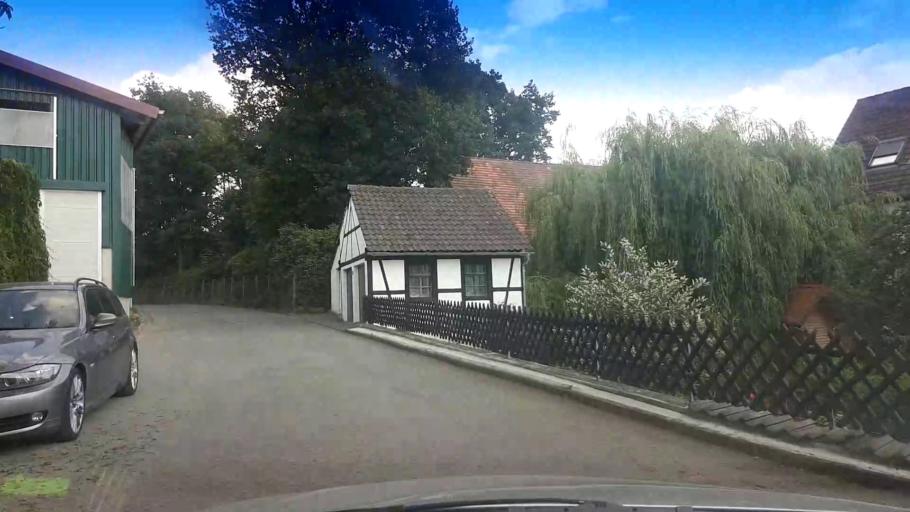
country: DE
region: Bavaria
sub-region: Upper Franconia
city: Zapfendorf
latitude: 50.0190
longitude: 10.9349
